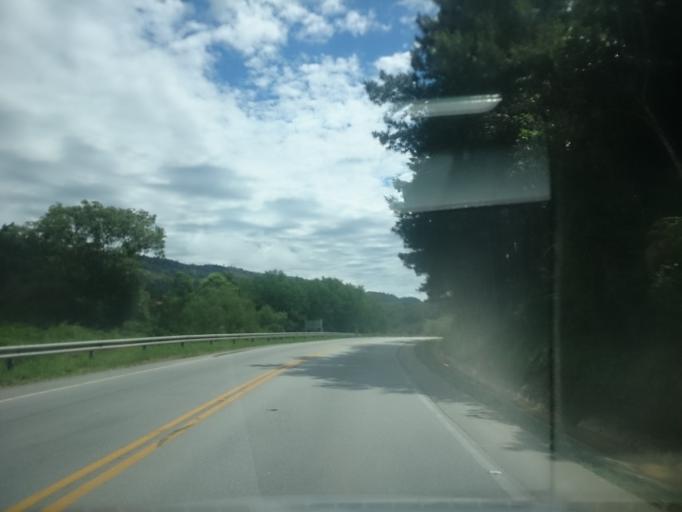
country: BR
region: Santa Catarina
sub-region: Anitapolis
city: Anitapolis
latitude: -27.7128
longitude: -49.2501
